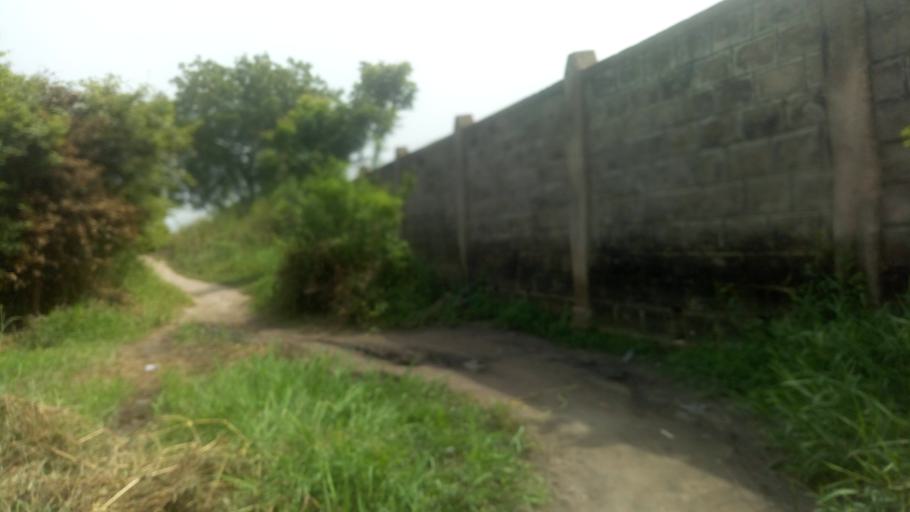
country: TG
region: Maritime
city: Lome
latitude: 6.2799
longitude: 1.2047
